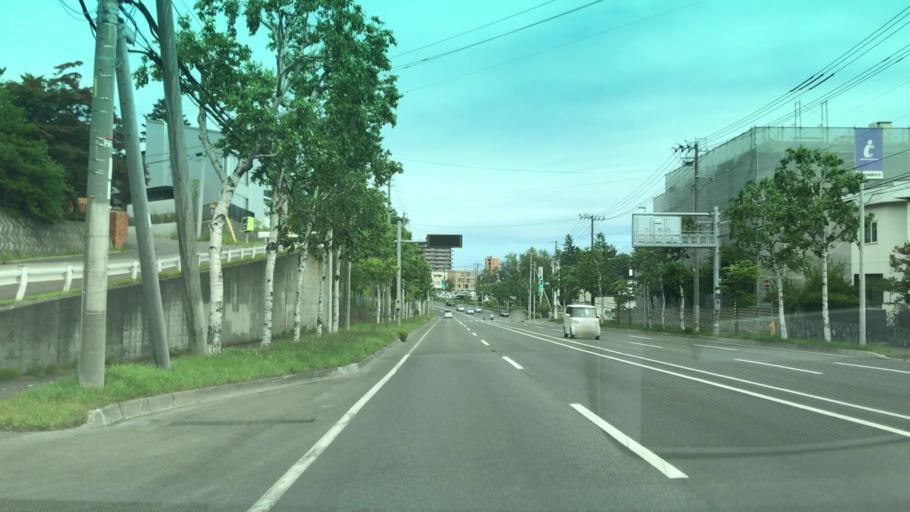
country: JP
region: Hokkaido
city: Sapporo
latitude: 43.0677
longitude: 141.2881
